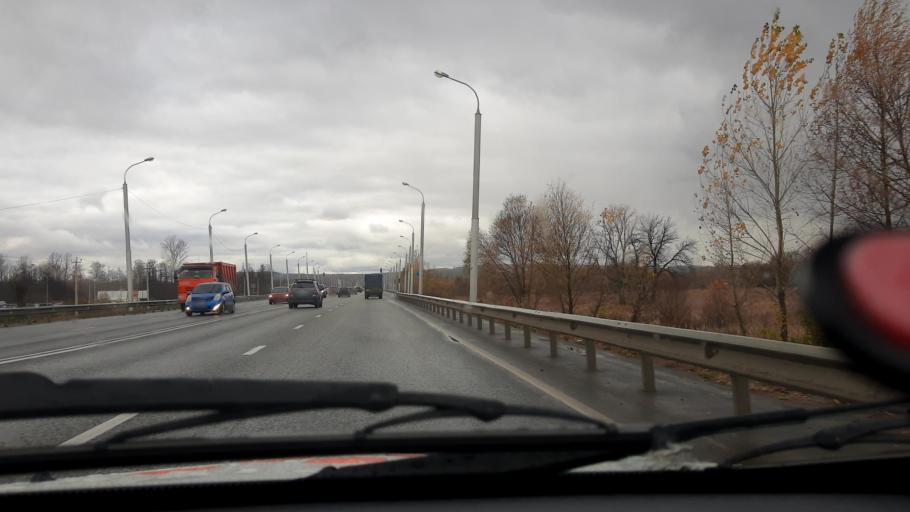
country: RU
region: Bashkortostan
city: Ufa
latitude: 54.8037
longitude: 56.1867
